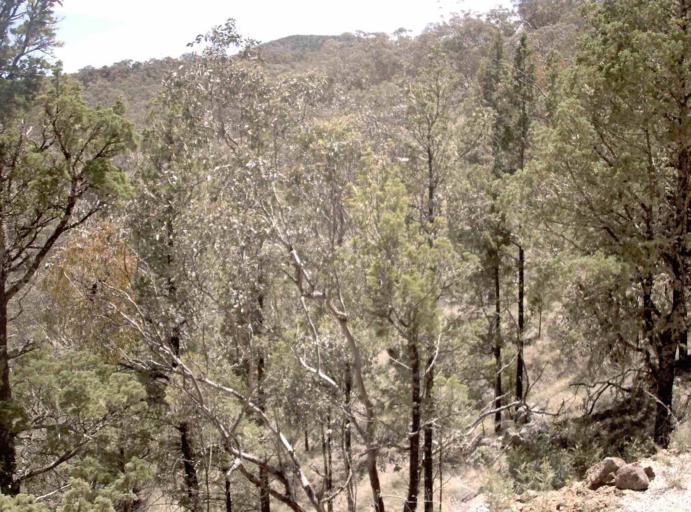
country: AU
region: New South Wales
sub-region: Snowy River
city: Jindabyne
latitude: -36.9467
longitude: 148.3381
